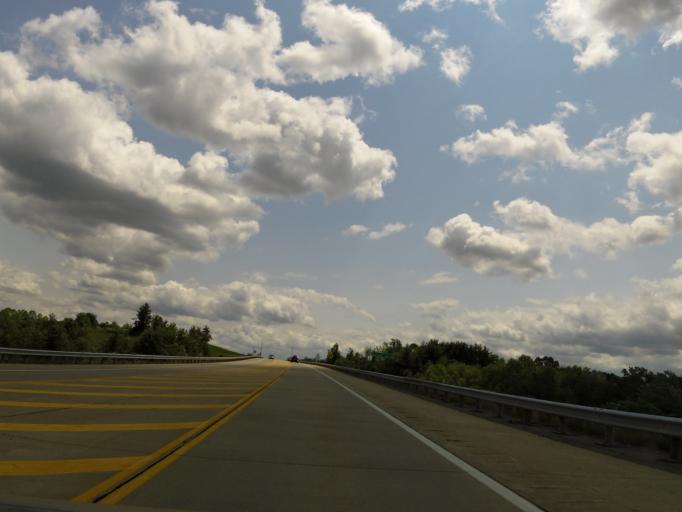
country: US
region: Ohio
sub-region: Athens County
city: Athens
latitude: 39.2744
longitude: -82.0954
